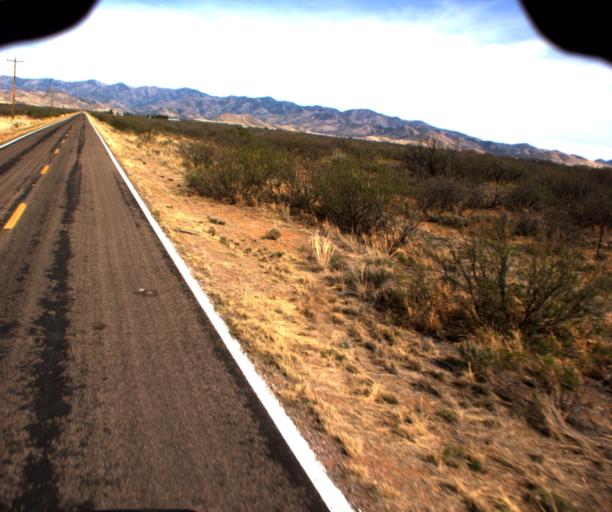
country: US
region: Arizona
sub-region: Cochise County
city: Willcox
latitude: 31.8760
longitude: -109.5173
